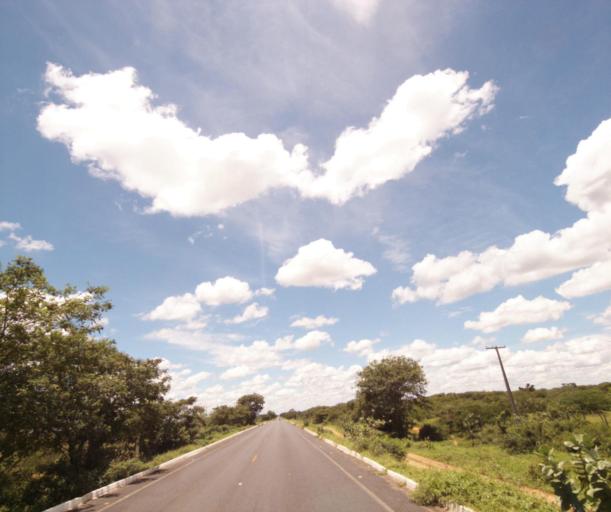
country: BR
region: Bahia
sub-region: Bom Jesus Da Lapa
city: Bom Jesus da Lapa
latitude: -13.2583
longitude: -43.4747
